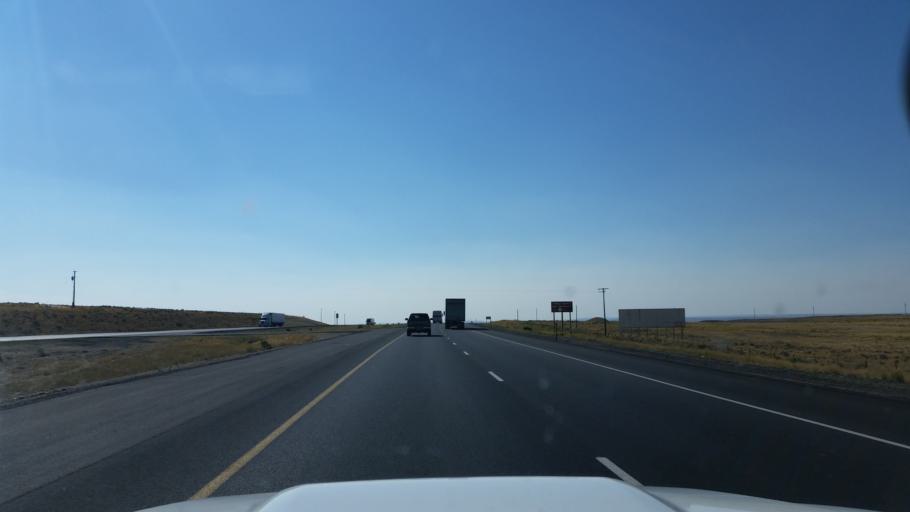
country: US
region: Wyoming
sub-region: Sweetwater County
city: Green River
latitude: 41.5423
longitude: -109.8921
